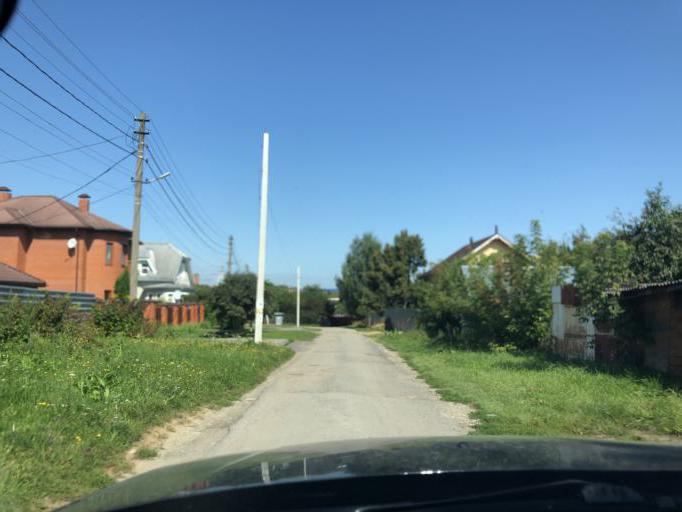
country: RU
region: Tula
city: Mendeleyevskiy
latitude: 54.1798
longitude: 37.5508
